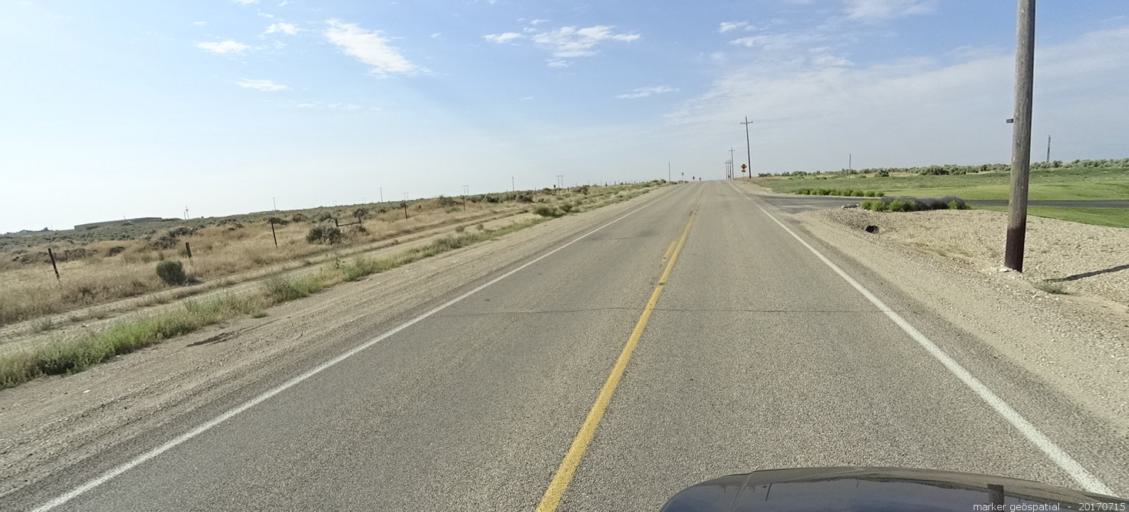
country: US
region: Idaho
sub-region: Ada County
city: Boise
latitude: 43.4618
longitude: -116.2344
